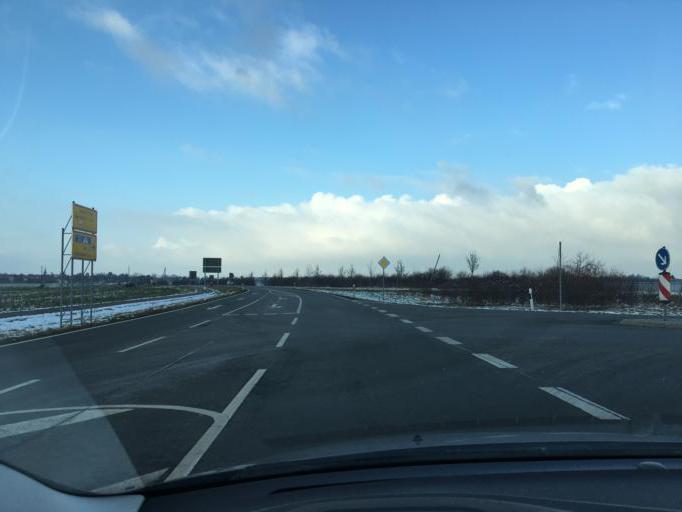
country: DE
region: Saxony
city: Brandis
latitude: 51.3440
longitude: 12.5974
